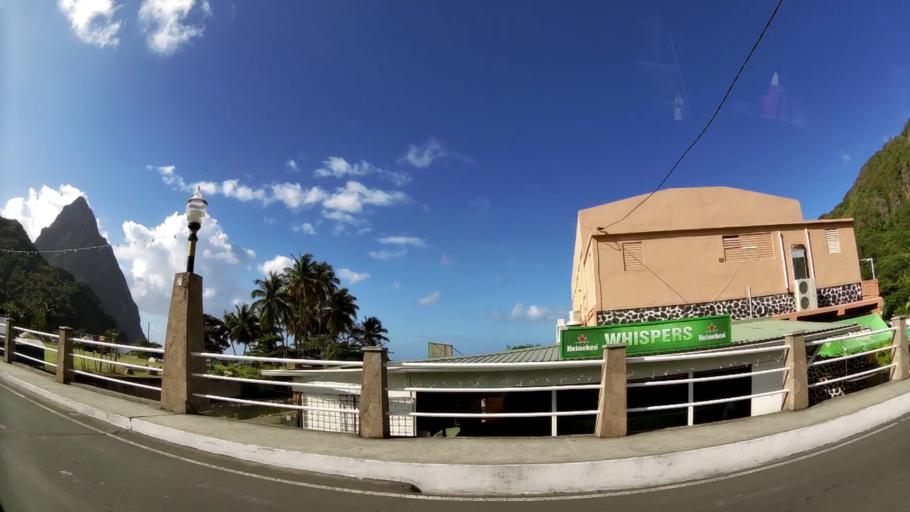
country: LC
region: Soufriere
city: Soufriere
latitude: 13.8564
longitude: -61.0600
